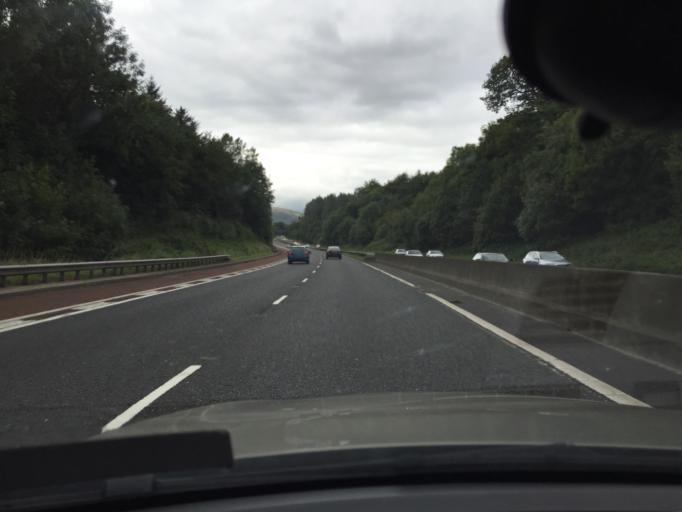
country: GB
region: Northern Ireland
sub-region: Lisburn District
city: Lisburn
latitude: 54.5438
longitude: -5.9938
